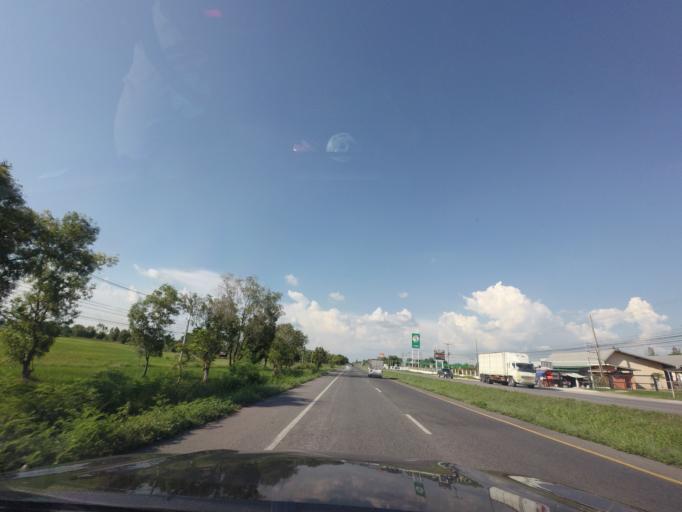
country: TH
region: Khon Kaen
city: Non Sila
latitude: 15.9924
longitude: 102.6993
